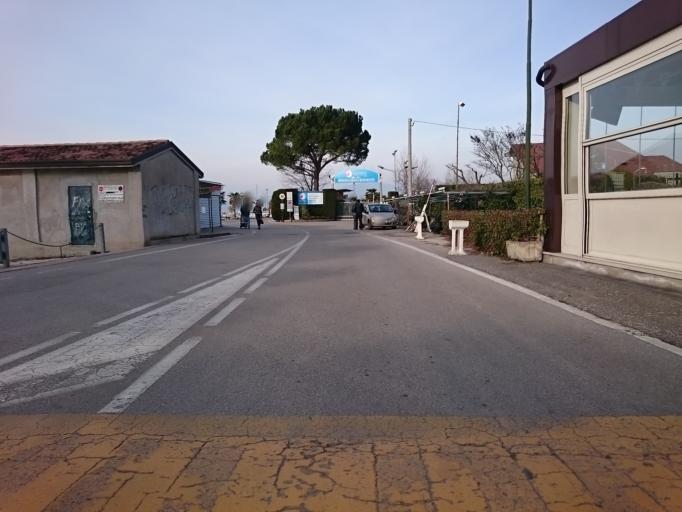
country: IT
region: Veneto
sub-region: Provincia di Verona
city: Peschiera del Garda
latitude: 45.4447
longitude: 10.6944
